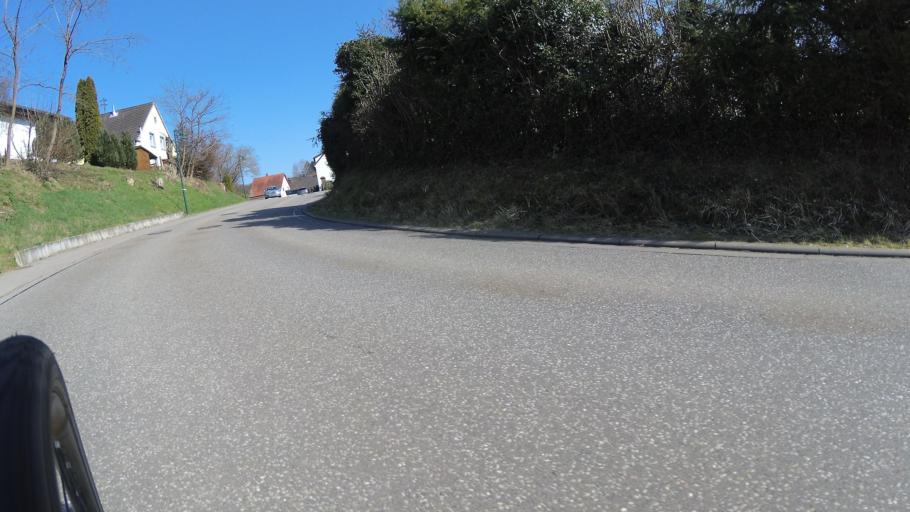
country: DE
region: Rheinland-Pfalz
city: Ruthweiler
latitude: 49.5467
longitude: 7.3857
